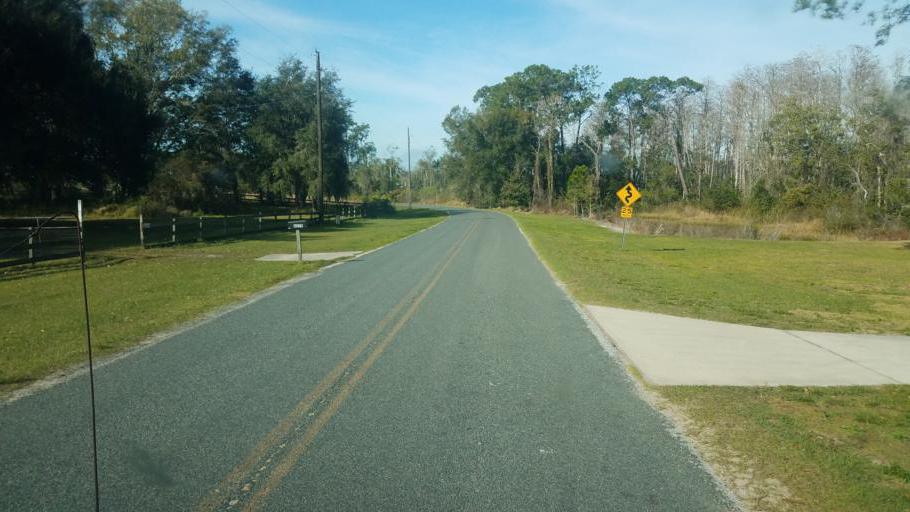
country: US
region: Florida
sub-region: Lake County
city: Clermont
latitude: 28.4452
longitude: -81.7898
